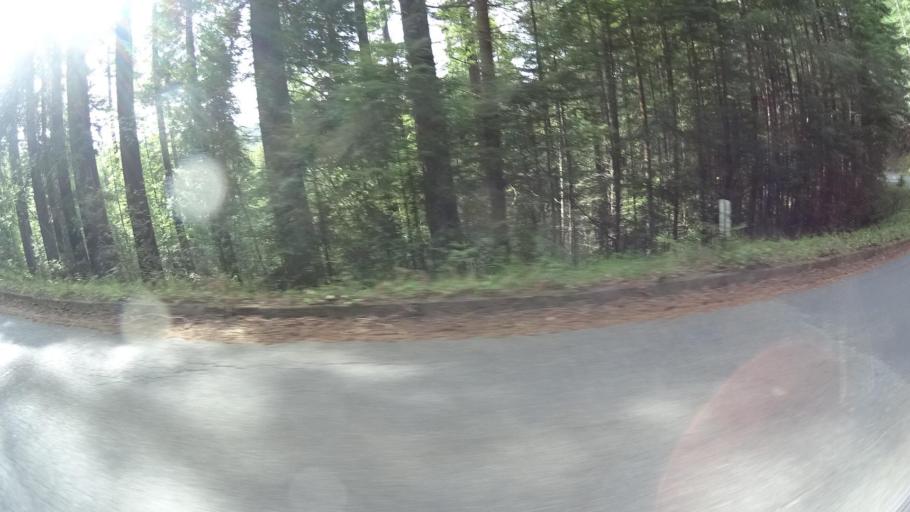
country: US
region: California
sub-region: Humboldt County
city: Bayside
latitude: 40.7566
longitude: -124.0358
